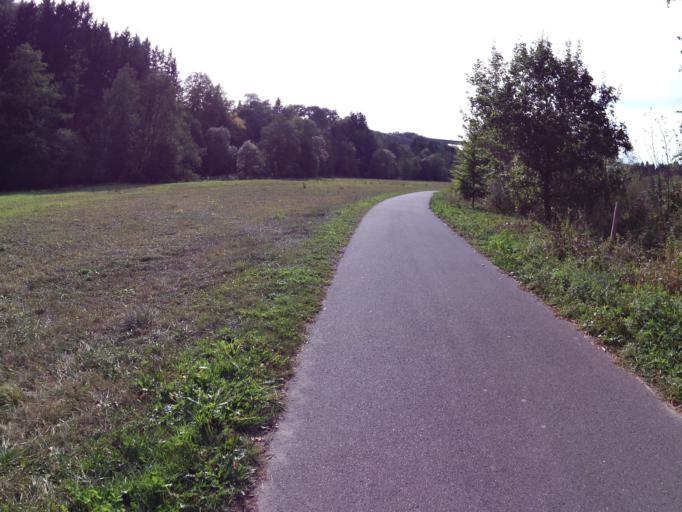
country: DE
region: Rheinland-Pfalz
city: Winterspelt
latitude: 50.2374
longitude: 6.1955
